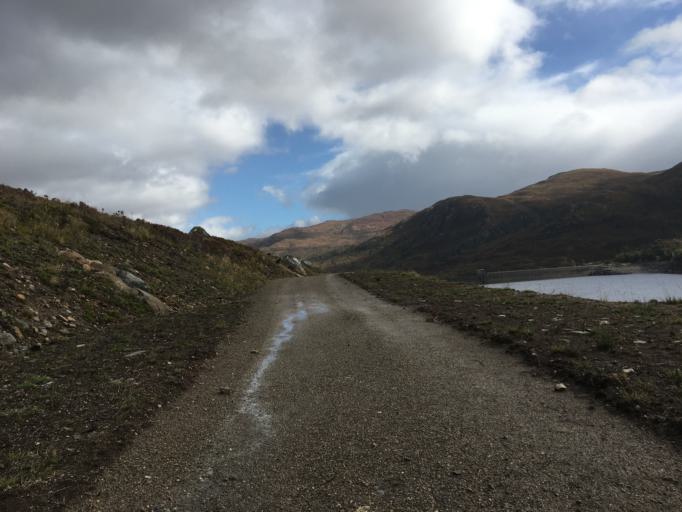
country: GB
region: Scotland
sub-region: Highland
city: Spean Bridge
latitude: 57.3399
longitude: -4.9675
